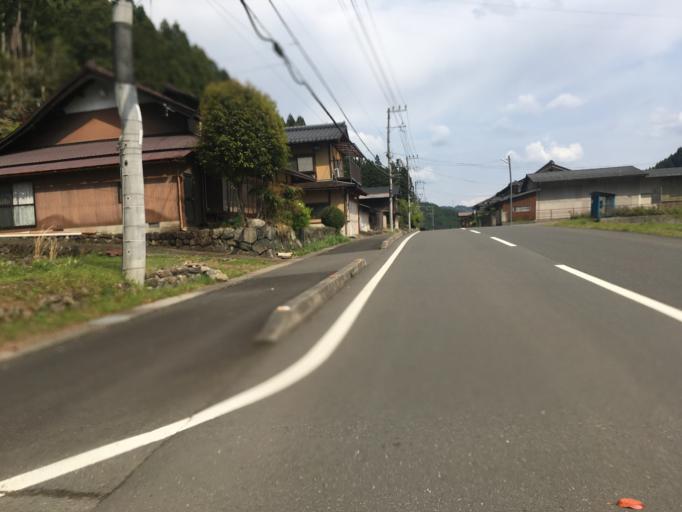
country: JP
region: Kyoto
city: Kameoka
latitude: 35.1450
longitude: 135.5805
